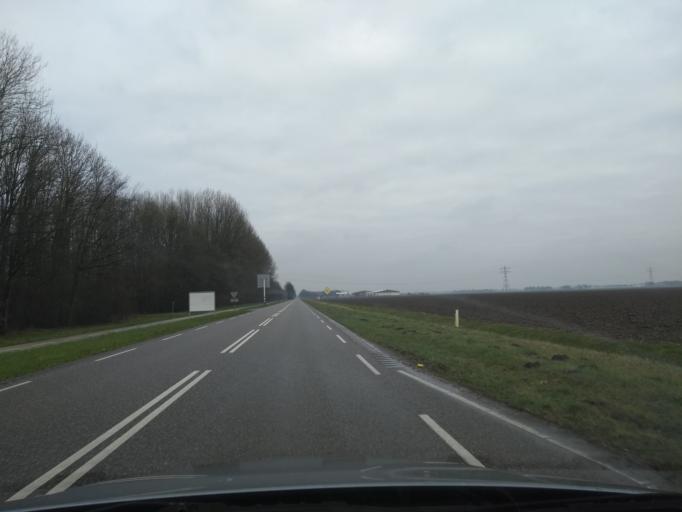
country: NL
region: Overijssel
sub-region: Gemeente Steenwijkerland
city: Vollenhove
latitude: 52.6864
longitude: 5.9418
